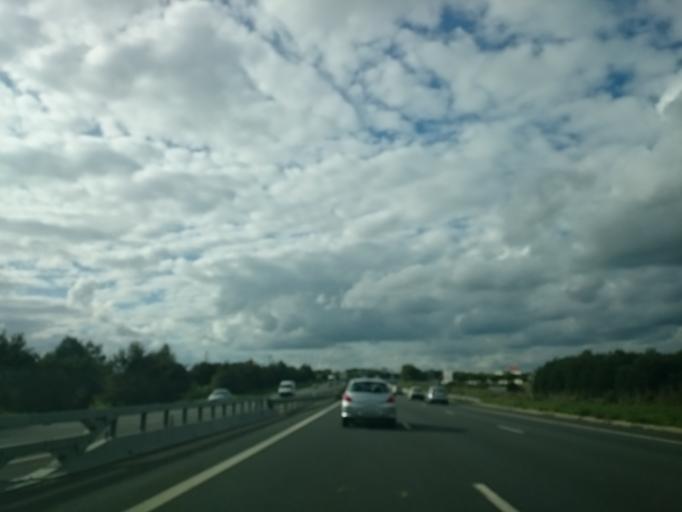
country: FR
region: Brittany
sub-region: Departement d'Ille-et-Vilaine
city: Pace
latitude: 48.1345
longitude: -1.7635
